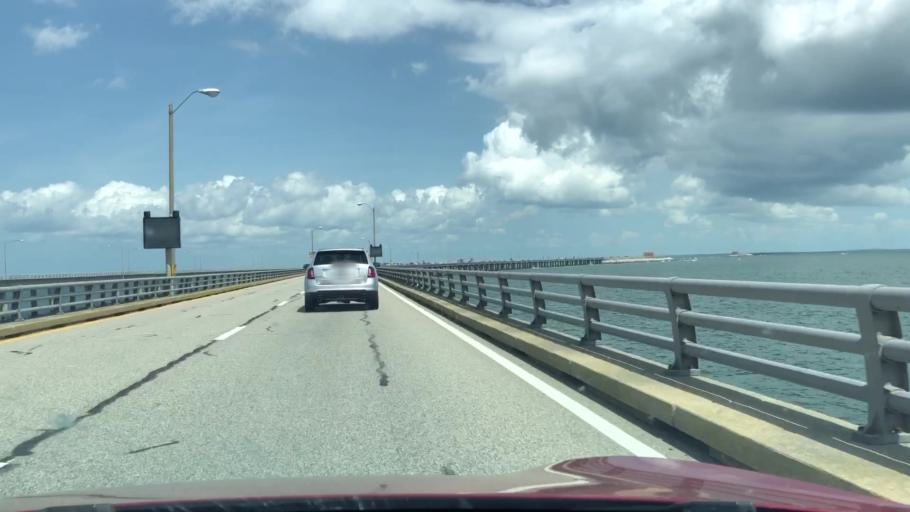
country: US
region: Virginia
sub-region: City of Virginia Beach
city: Virginia Beach
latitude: 37.0242
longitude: -76.0887
